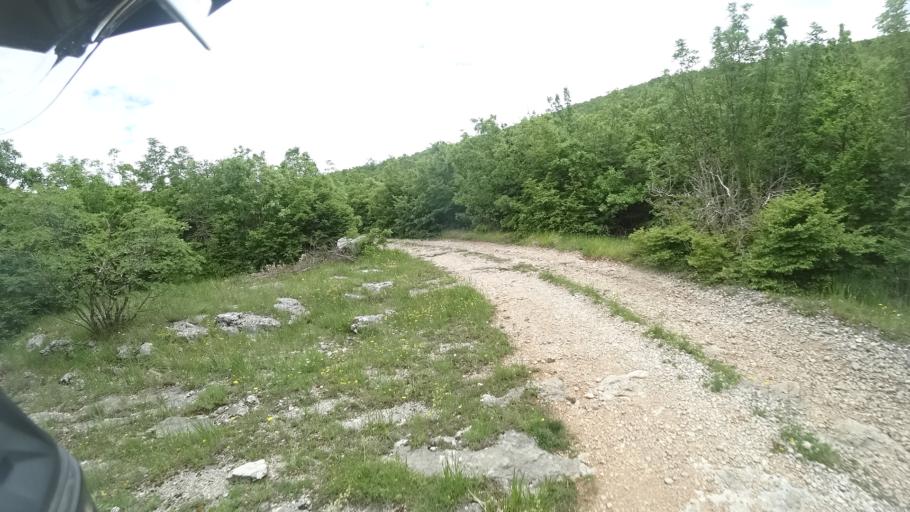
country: HR
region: Splitsko-Dalmatinska
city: Hrvace
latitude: 43.8942
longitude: 16.5422
